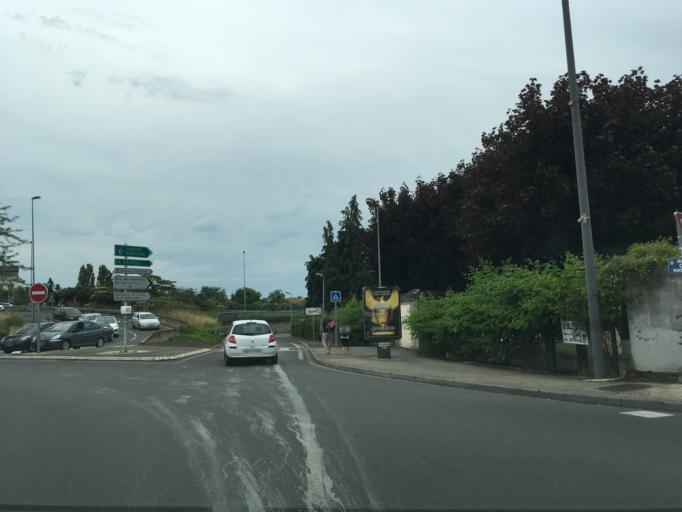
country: FR
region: Poitou-Charentes
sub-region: Departement des Deux-Sevres
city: Niort
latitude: 46.3350
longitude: -0.4728
